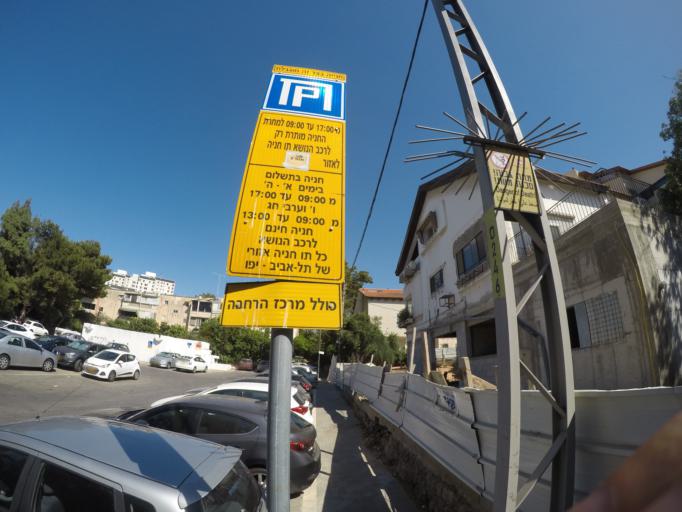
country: IL
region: Tel Aviv
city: Ramat Gan
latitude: 32.1079
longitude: 34.7999
